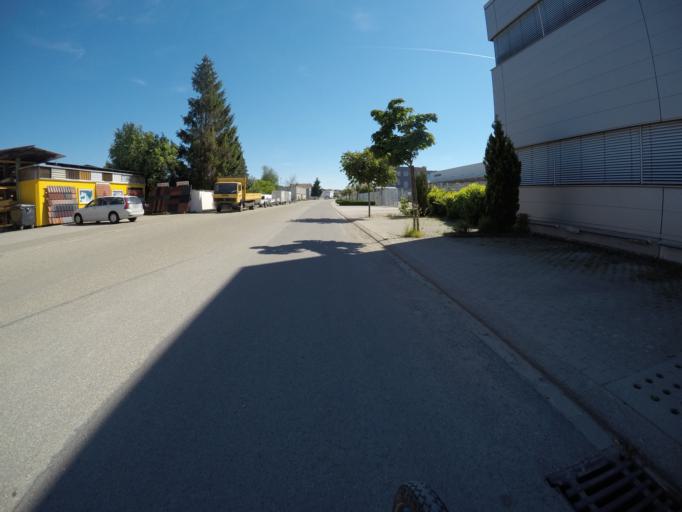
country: DE
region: Baden-Wuerttemberg
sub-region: Karlsruhe Region
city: Konigsbach-Stein
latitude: 48.9632
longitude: 8.5947
